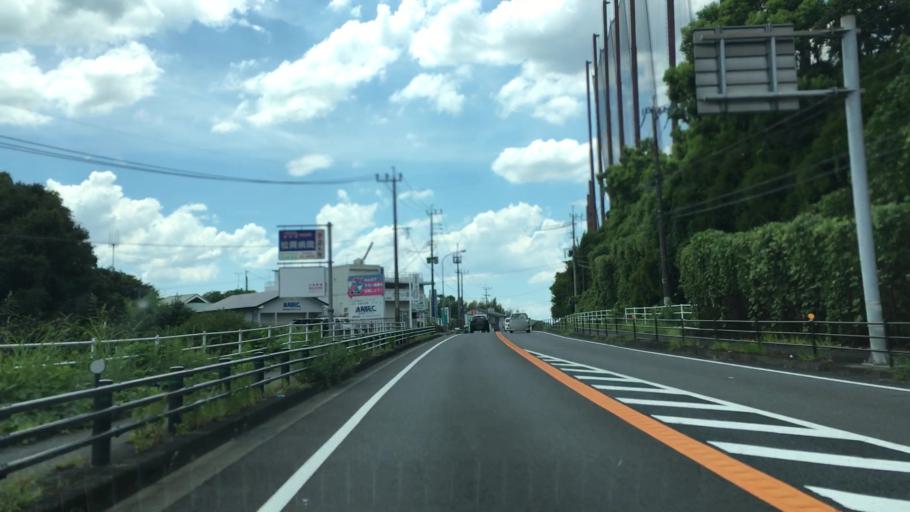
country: JP
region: Saga Prefecture
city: Tosu
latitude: 33.3591
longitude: 130.4929
